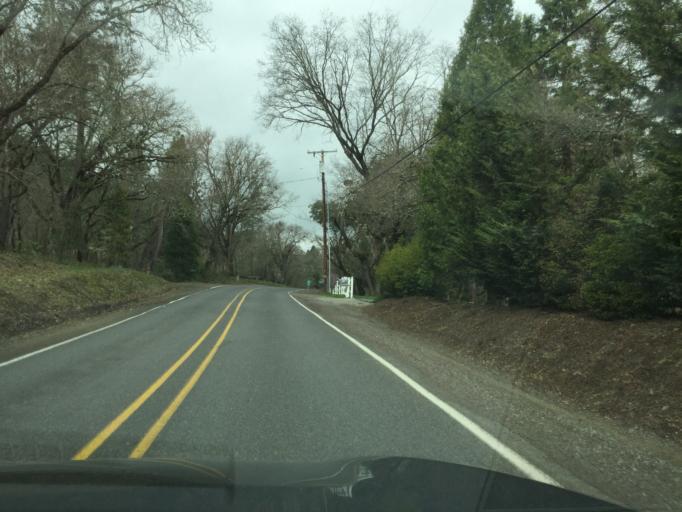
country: US
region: Oregon
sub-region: Jackson County
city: Central Point
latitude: 42.3765
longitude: -122.9554
